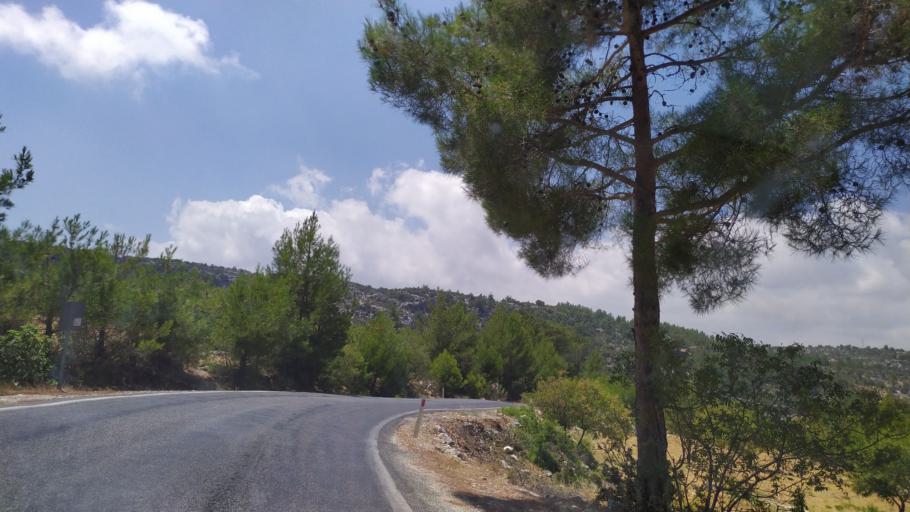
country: TR
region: Mersin
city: Gulnar
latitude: 36.2755
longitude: 33.3875
